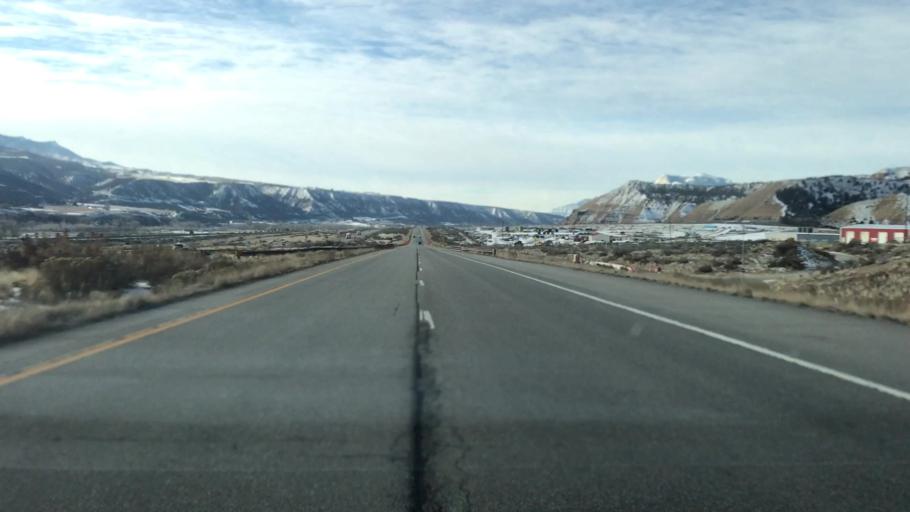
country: US
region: Colorado
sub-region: Garfield County
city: Battlement Mesa
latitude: 39.4988
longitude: -107.9407
